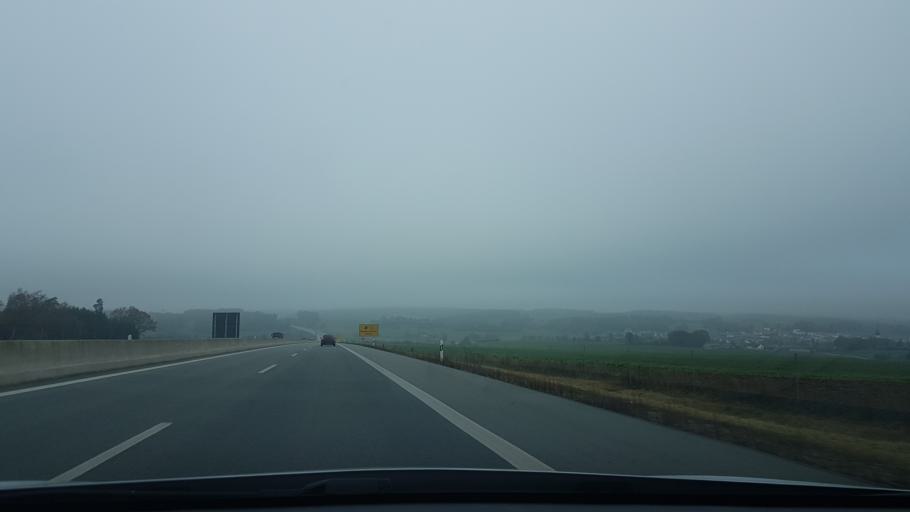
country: DE
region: Bavaria
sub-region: Lower Bavaria
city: Ergoldsbach
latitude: 48.7191
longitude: 12.1667
